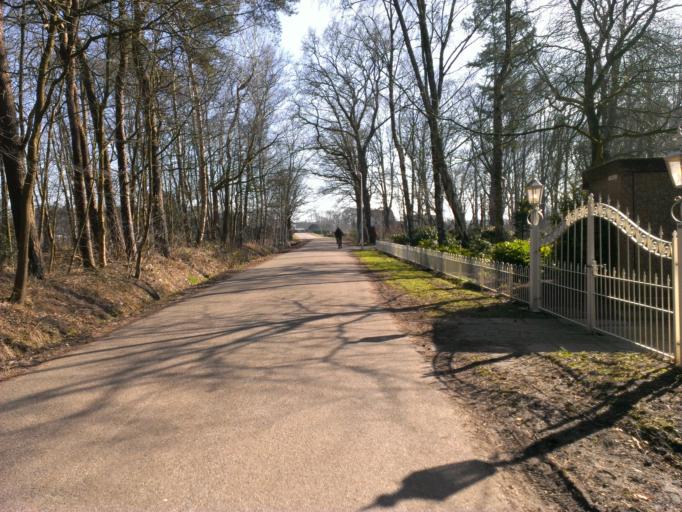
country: NL
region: Overijssel
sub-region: Gemeente Almelo
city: Almelo
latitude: 52.3266
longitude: 6.6854
